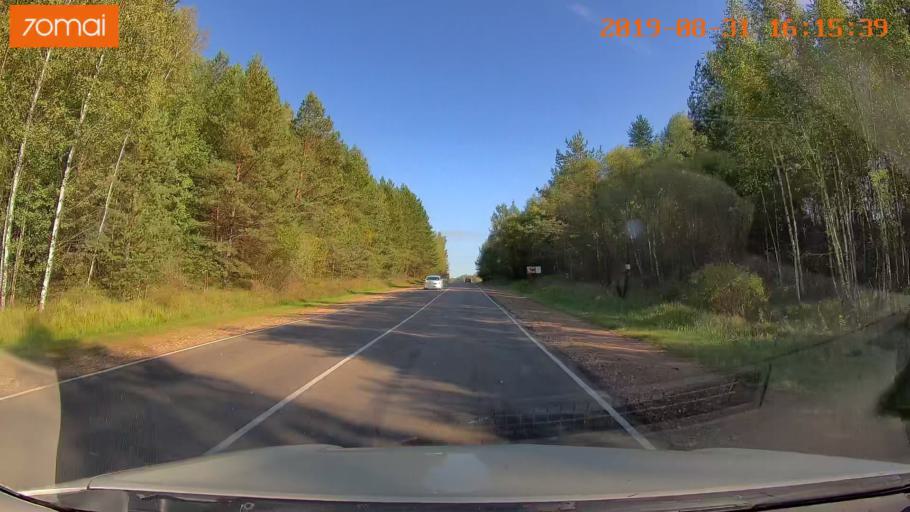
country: RU
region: Kaluga
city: Nikola-Lenivets
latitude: 54.5584
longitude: 35.4919
